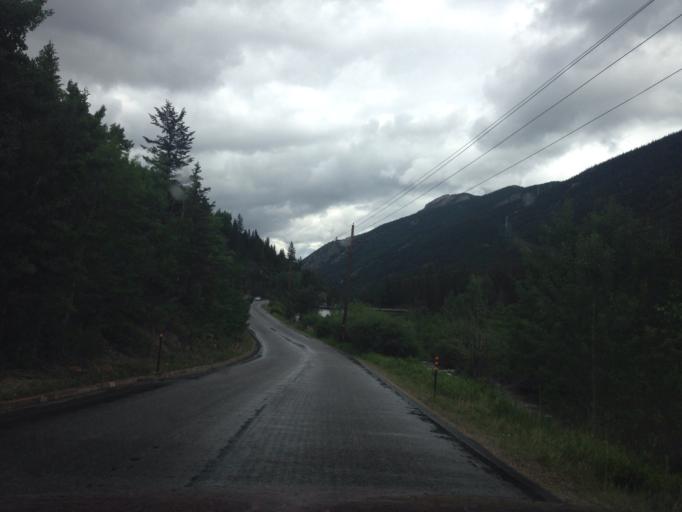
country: US
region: Colorado
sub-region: Clear Creek County
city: Georgetown
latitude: 39.6899
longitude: -105.6990
